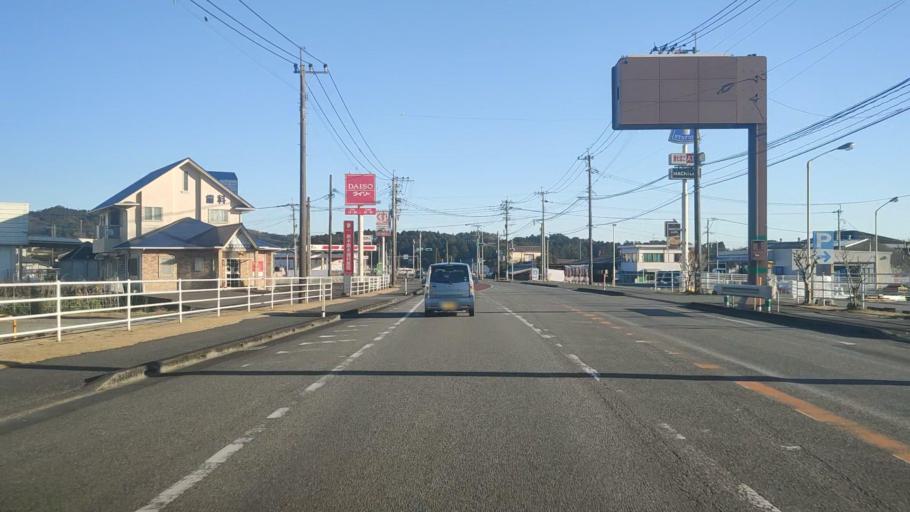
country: JP
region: Miyazaki
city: Takanabe
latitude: 32.2571
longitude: 131.5556
